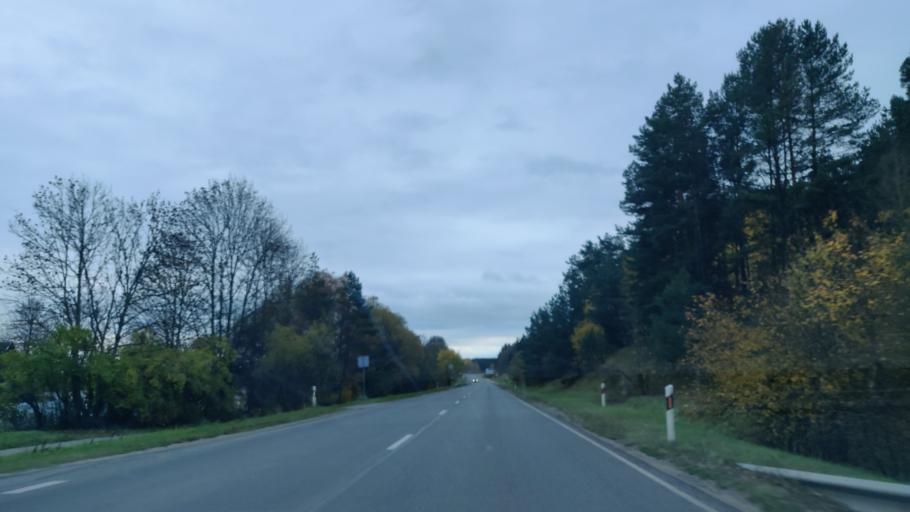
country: LT
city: Trakai
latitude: 54.6578
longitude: 24.9160
